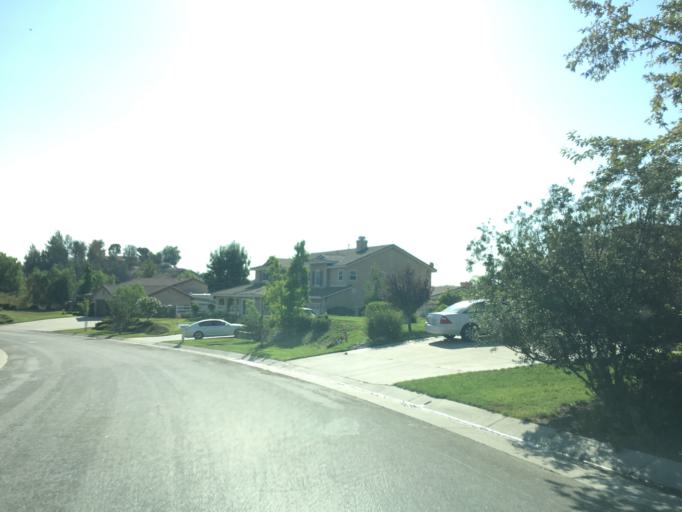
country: US
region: California
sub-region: Los Angeles County
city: Val Verde
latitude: 34.4664
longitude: -118.6674
